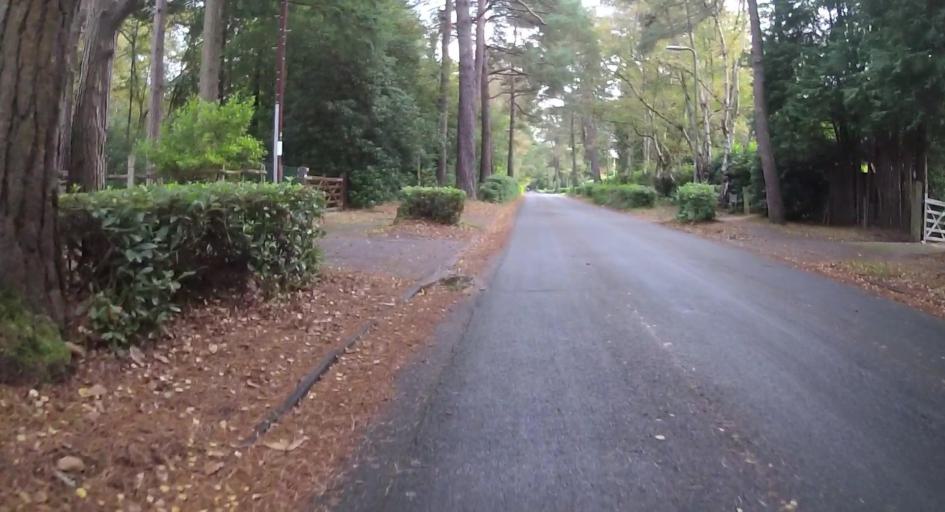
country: GB
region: England
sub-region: Hampshire
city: Fleet
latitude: 51.2823
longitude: -0.8575
